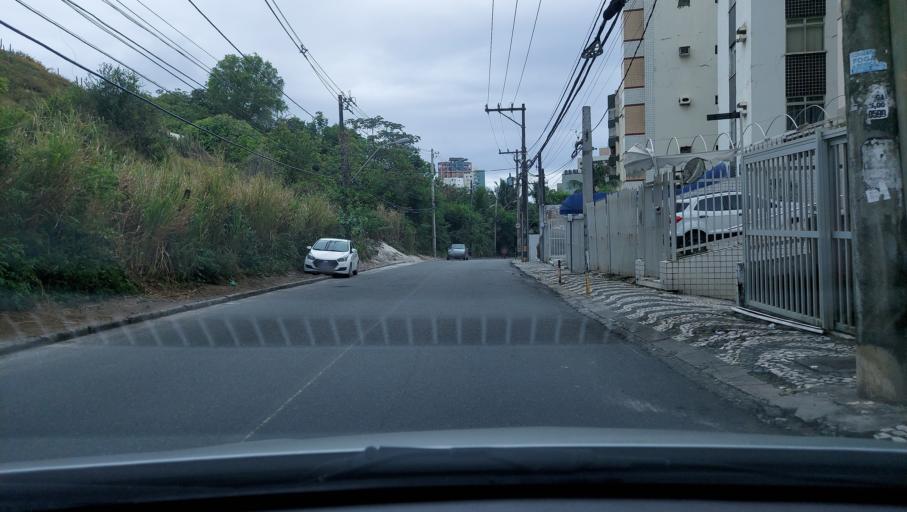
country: BR
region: Bahia
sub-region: Salvador
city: Salvador
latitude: -12.9869
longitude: -38.4438
